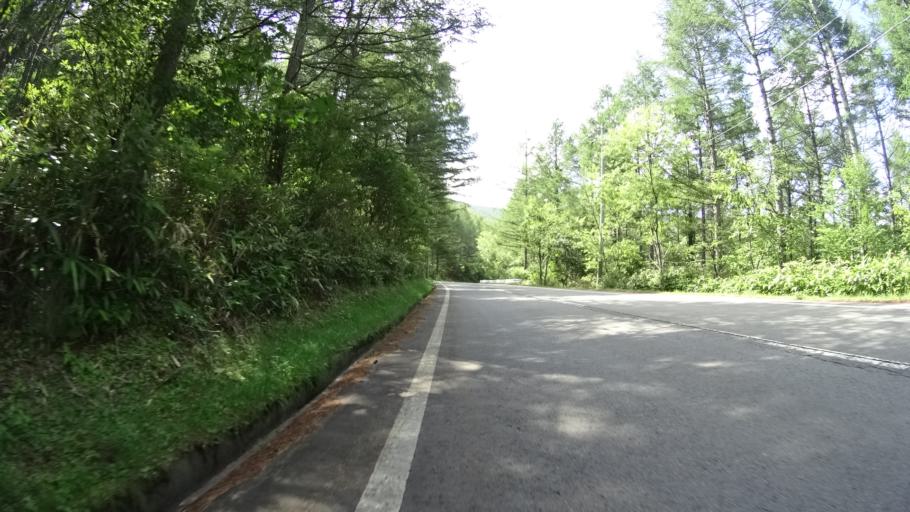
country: JP
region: Nagano
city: Saku
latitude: 36.0597
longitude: 138.3943
